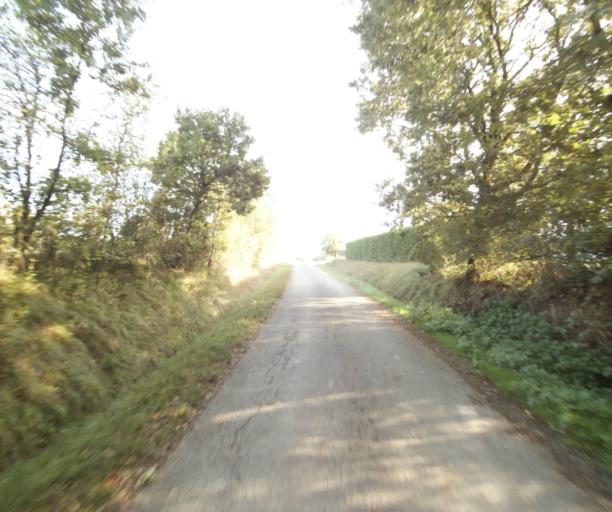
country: FR
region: Midi-Pyrenees
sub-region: Departement de la Haute-Garonne
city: Villemur-sur-Tarn
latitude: 43.9118
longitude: 1.5106
